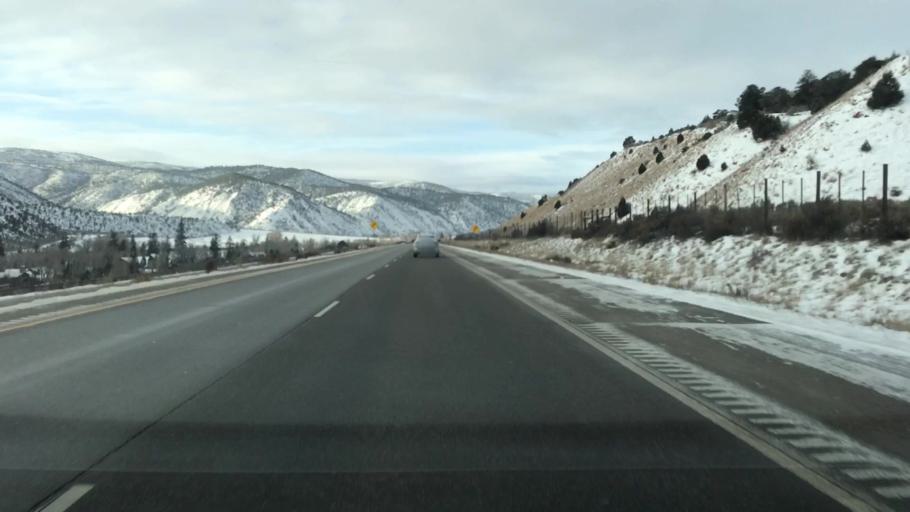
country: US
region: Colorado
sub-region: Eagle County
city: Eagle
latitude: 39.6884
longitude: -106.7516
